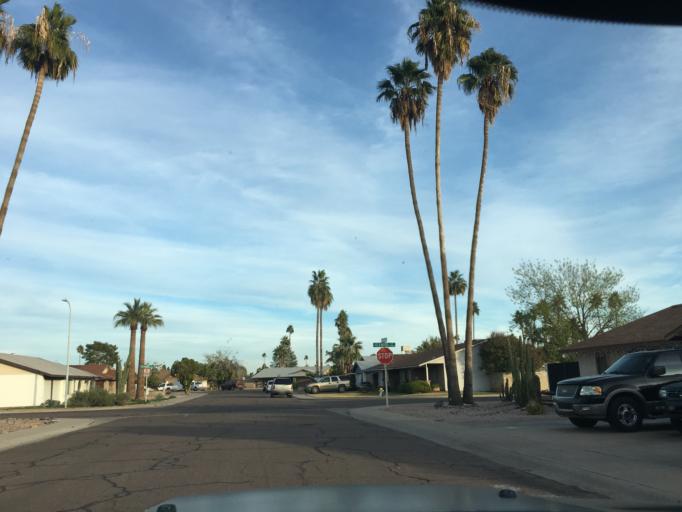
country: US
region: Arizona
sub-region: Maricopa County
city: Tempe
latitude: 33.3762
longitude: -111.9033
